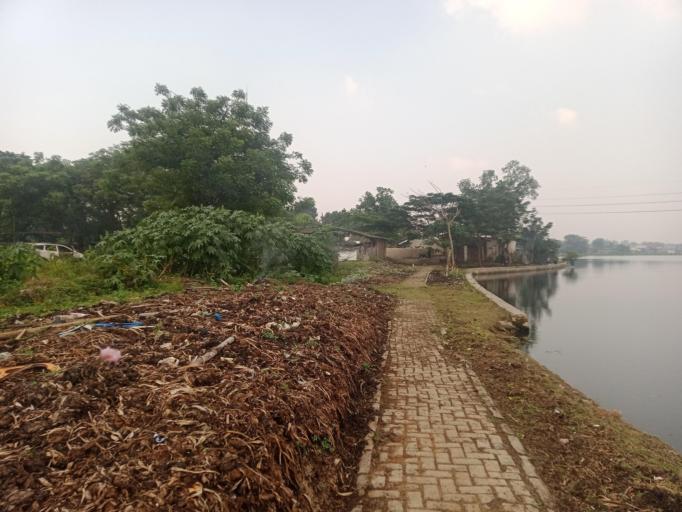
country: ID
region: West Java
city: Pasarkemis
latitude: -6.1715
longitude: 106.5226
